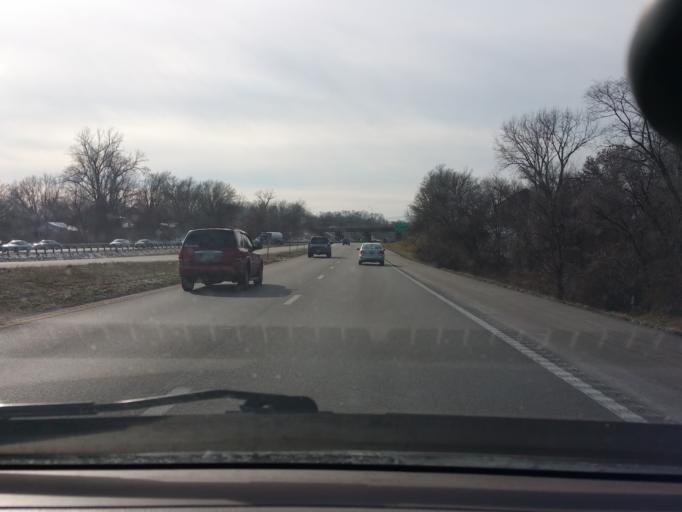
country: US
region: Missouri
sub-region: Clay County
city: Claycomo
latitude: 39.1859
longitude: -94.5186
